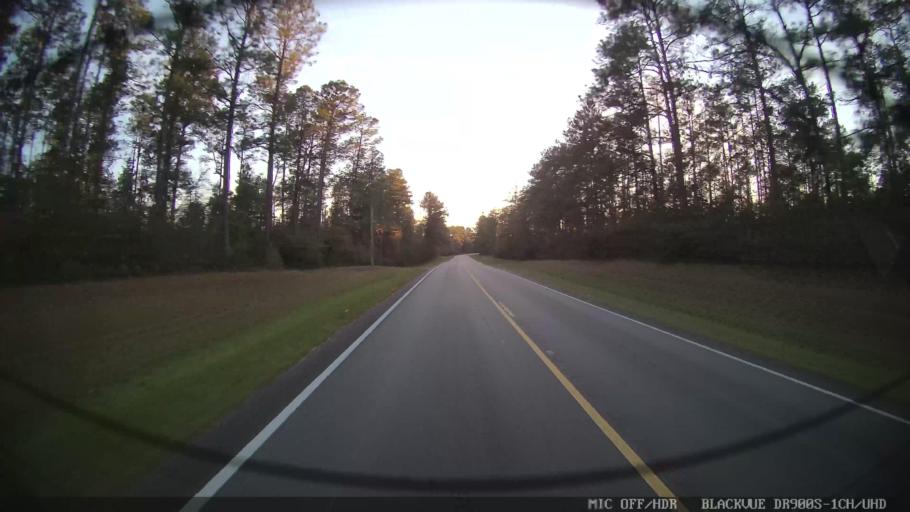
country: US
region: Mississippi
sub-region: Stone County
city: Wiggins
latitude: 31.0366
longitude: -89.2167
